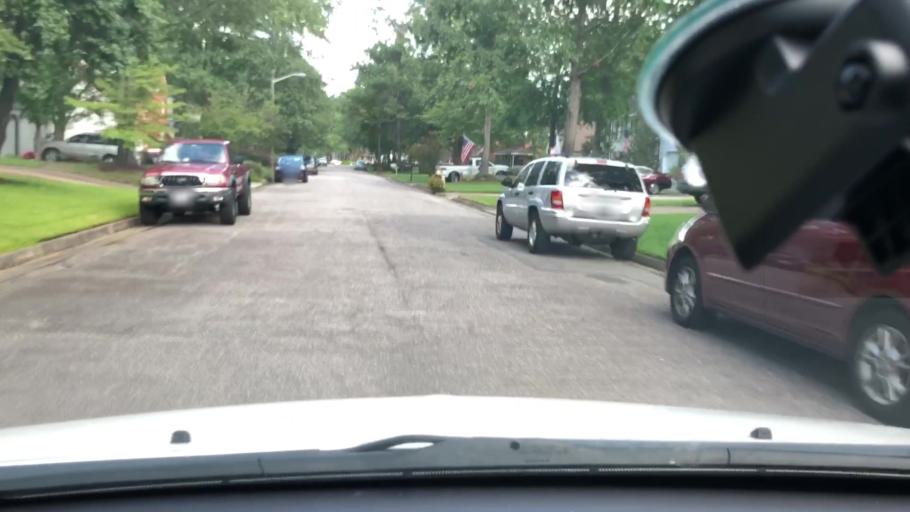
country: US
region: Virginia
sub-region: City of Chesapeake
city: Chesapeake
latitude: 36.7030
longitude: -76.2912
